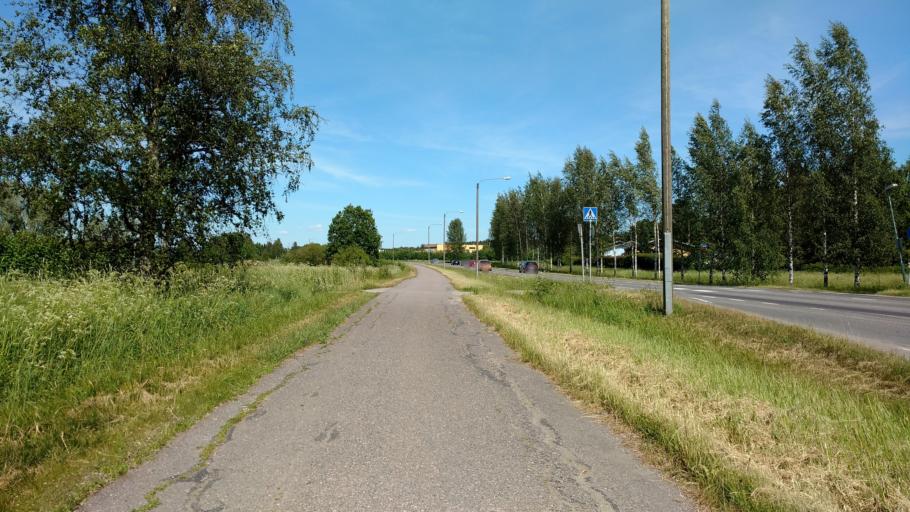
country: FI
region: Varsinais-Suomi
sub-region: Salo
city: Salo
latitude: 60.3954
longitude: 23.1525
